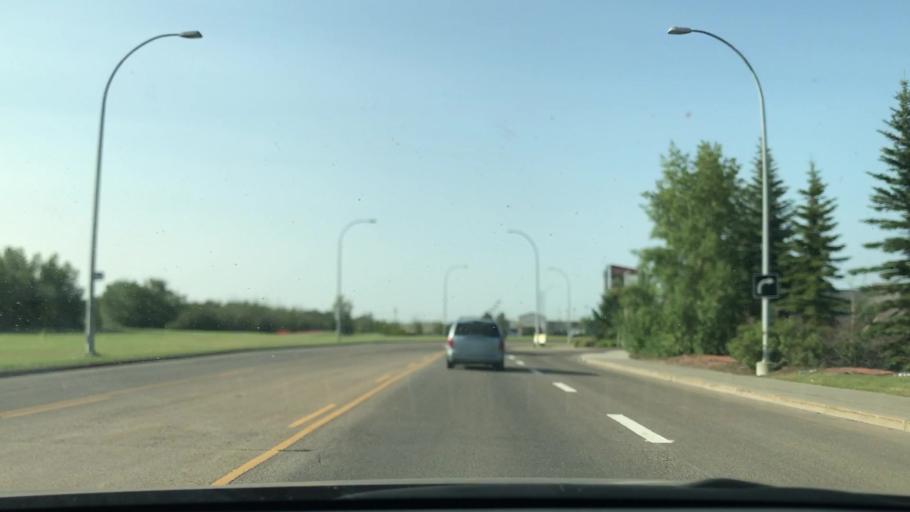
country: CA
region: Alberta
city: Edmonton
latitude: 53.4447
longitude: -113.4815
